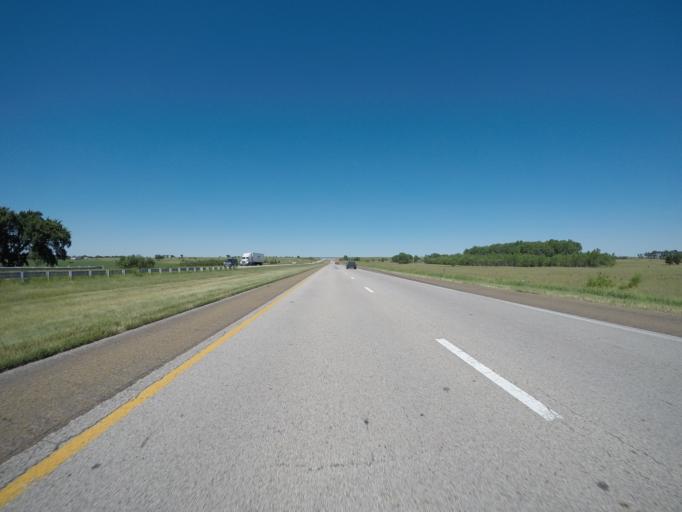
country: US
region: Kansas
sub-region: Lincoln County
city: Lincoln
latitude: 38.8780
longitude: -97.9021
